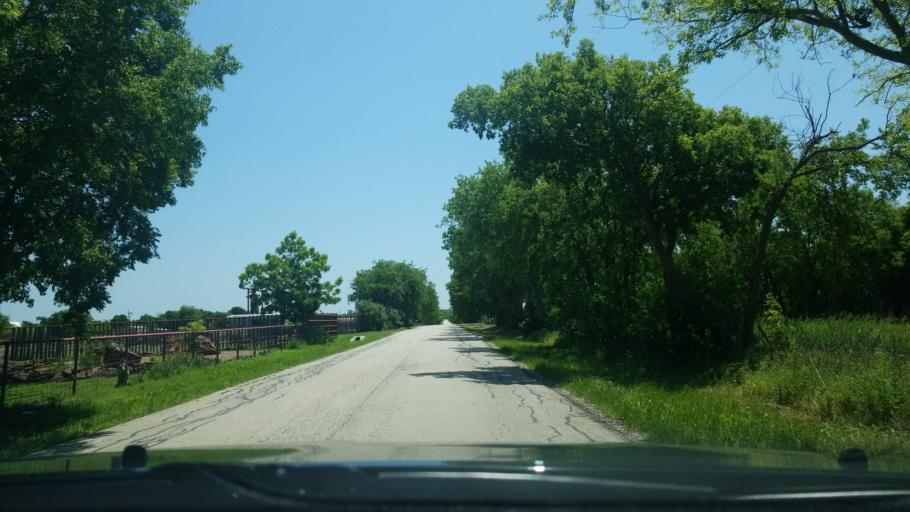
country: US
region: Texas
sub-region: Denton County
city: Krum
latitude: 33.2442
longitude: -97.2538
